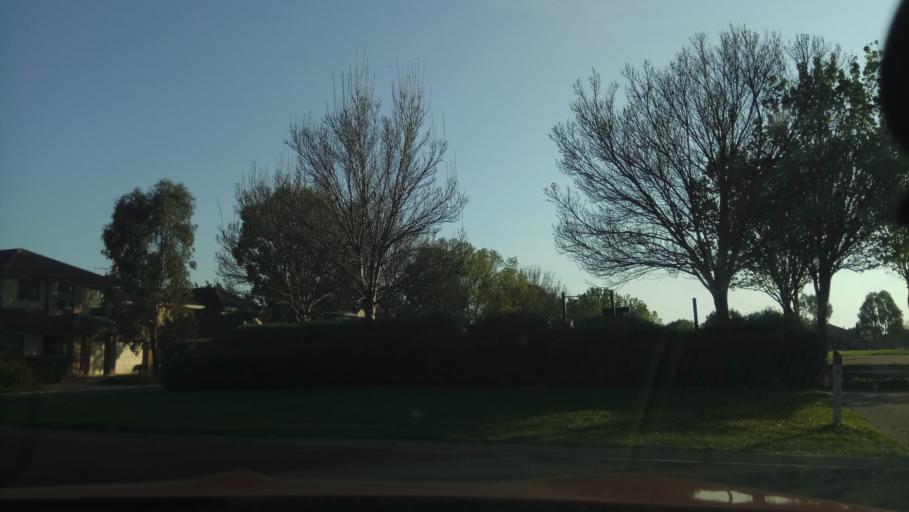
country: AU
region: Victoria
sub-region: Hobsons Bay
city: Altona Meadows
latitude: -37.8898
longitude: 144.7701
